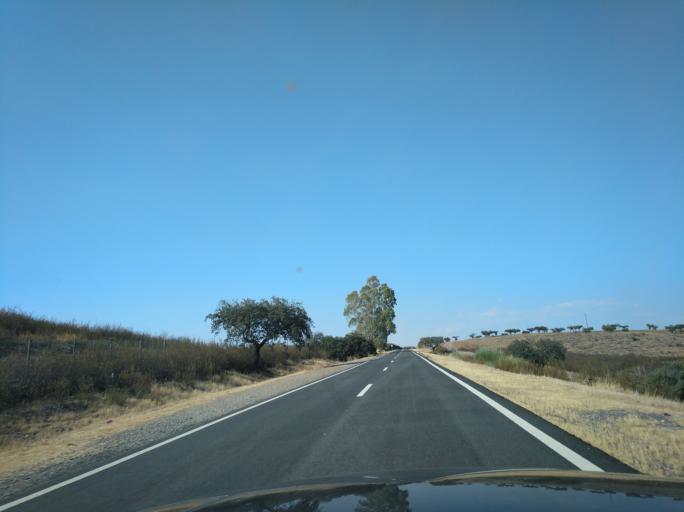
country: ES
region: Extremadura
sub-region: Provincia de Badajoz
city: Valencia del Mombuey
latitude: 38.1557
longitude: -7.2337
